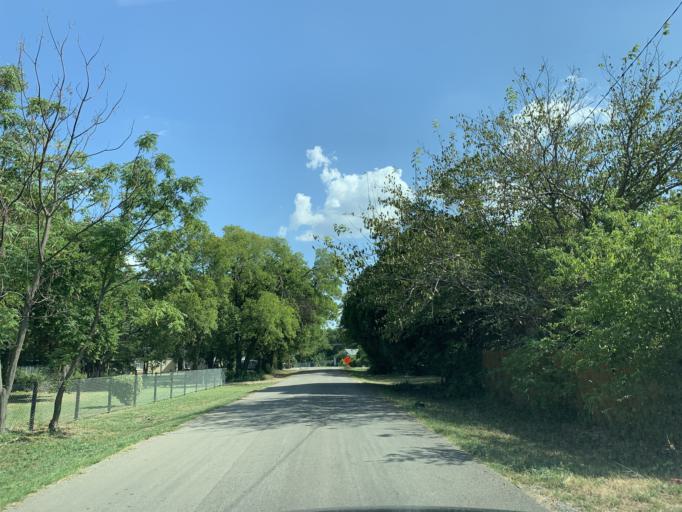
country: US
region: Texas
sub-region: Dallas County
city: Hutchins
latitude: 32.6539
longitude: -96.7732
